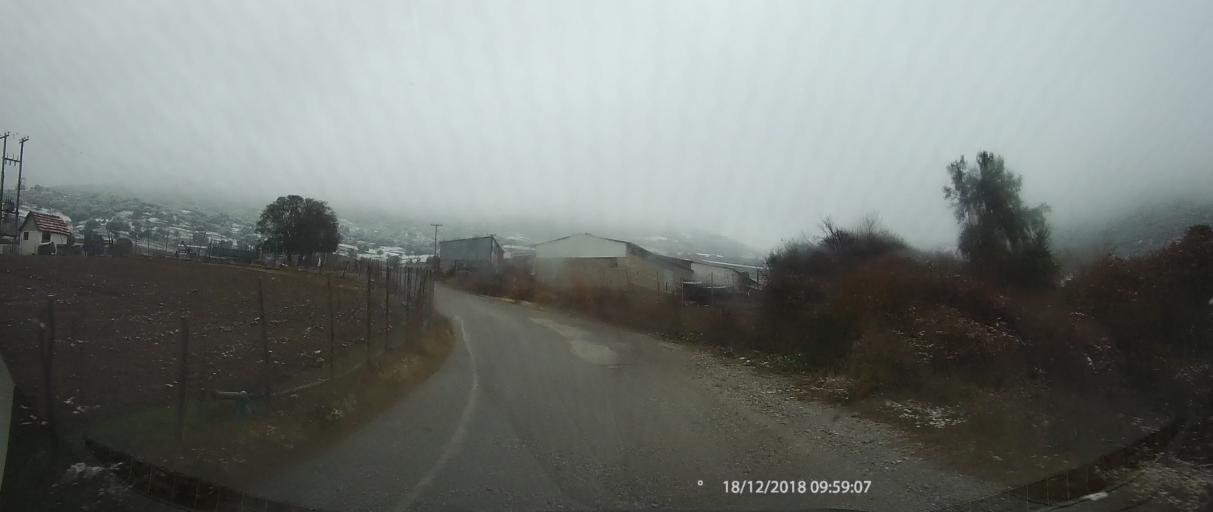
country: GR
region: Thessaly
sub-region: Nomos Larisis
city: Livadi
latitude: 40.0309
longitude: 22.2436
